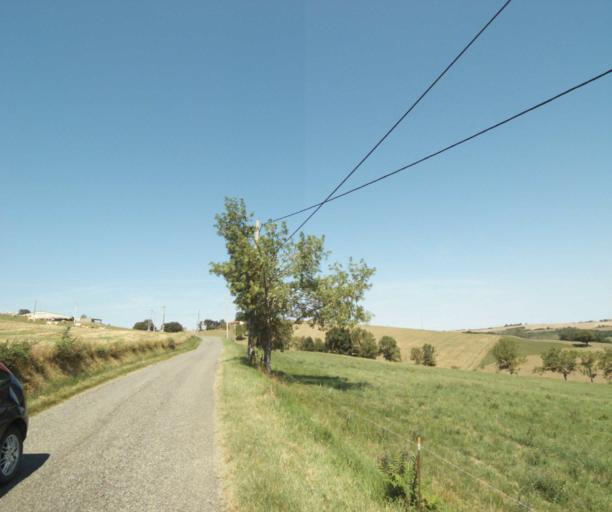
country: FR
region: Midi-Pyrenees
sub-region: Departement de l'Ariege
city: Lezat-sur-Leze
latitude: 43.2755
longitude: 1.3758
